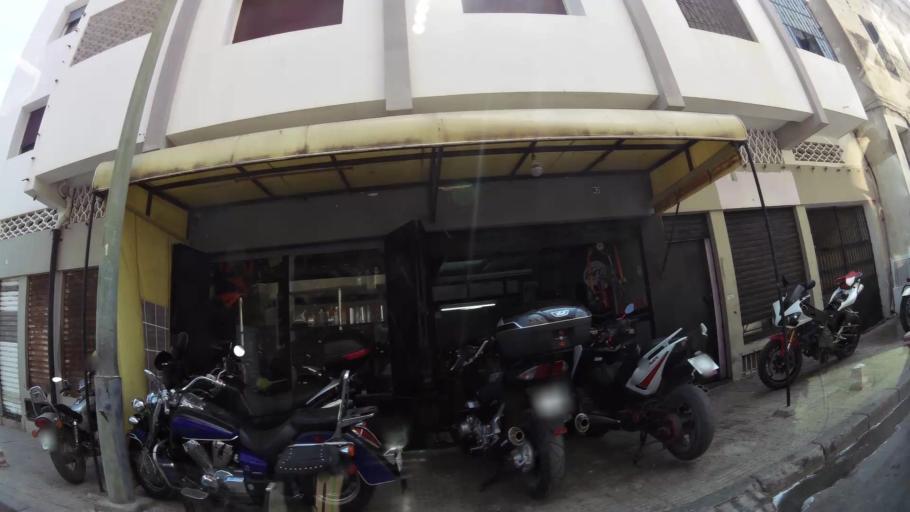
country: MA
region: Rabat-Sale-Zemmour-Zaer
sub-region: Rabat
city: Rabat
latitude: 34.0266
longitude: -6.8453
